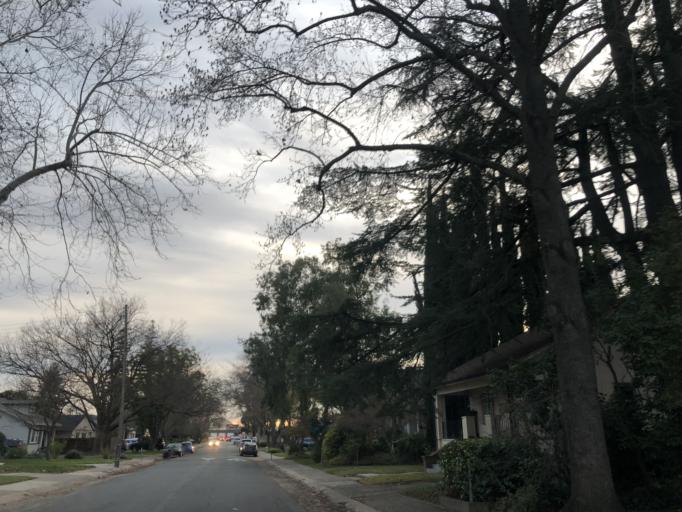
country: US
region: California
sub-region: Sacramento County
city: Sacramento
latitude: 38.5606
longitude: -121.4371
